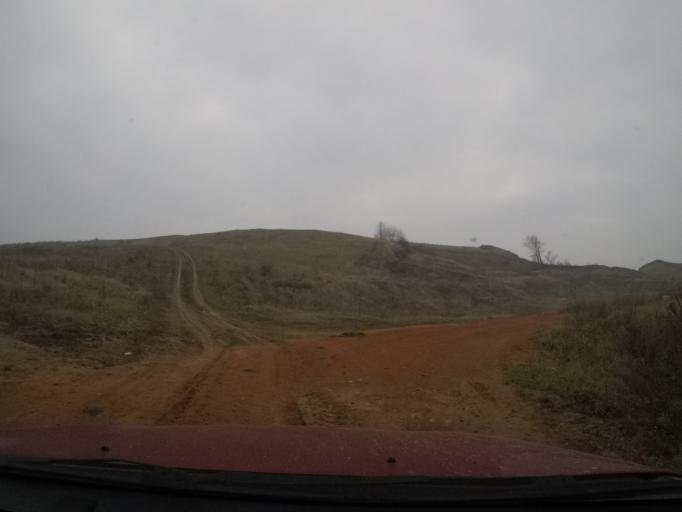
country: SK
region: Presovsky
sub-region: Okres Presov
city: Presov
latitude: 48.8822
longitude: 21.2772
